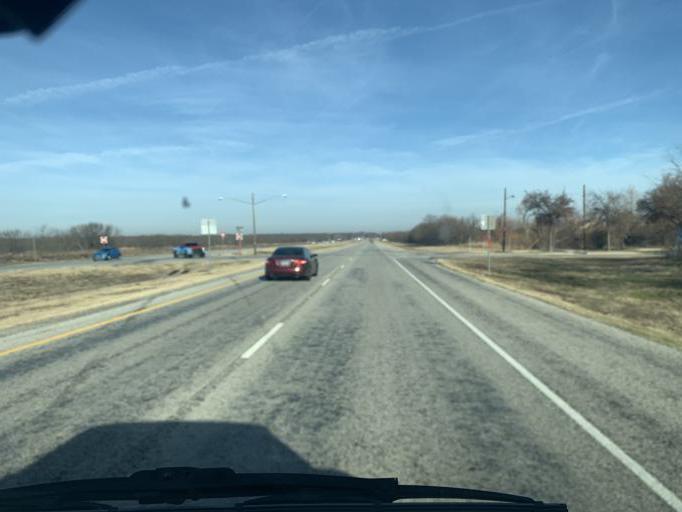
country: US
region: Texas
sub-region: Dallas County
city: Cedar Hill
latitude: 32.6508
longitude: -96.9770
